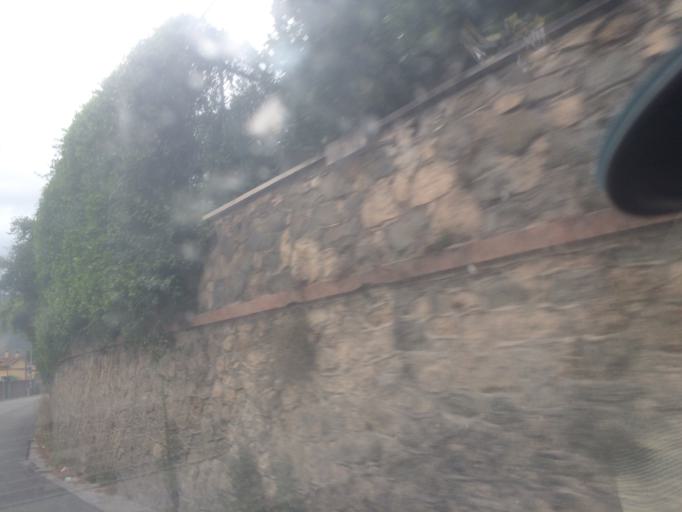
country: IT
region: Tuscany
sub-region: Provincia di Massa-Carrara
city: Carrara
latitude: 44.0651
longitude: 10.0837
